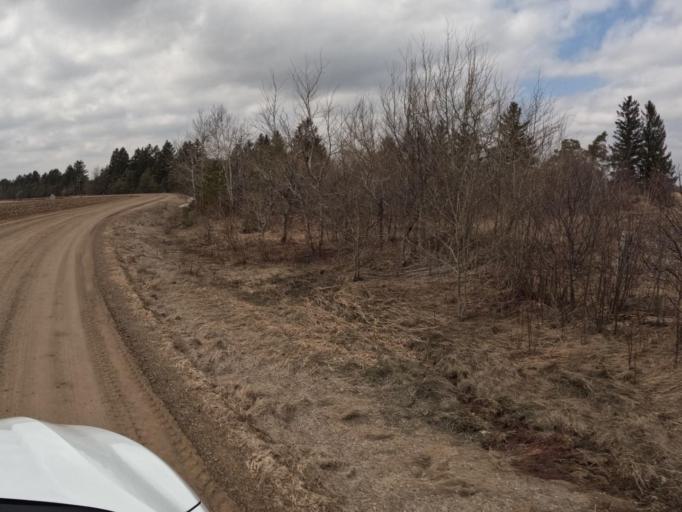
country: CA
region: Ontario
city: Shelburne
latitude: 44.0356
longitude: -80.2205
